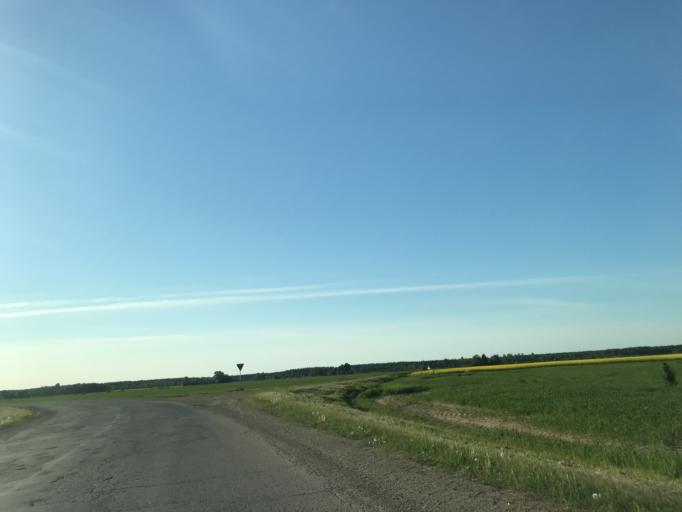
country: LV
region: Ozolnieku
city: Ozolnieki
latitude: 56.5724
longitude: 23.8471
